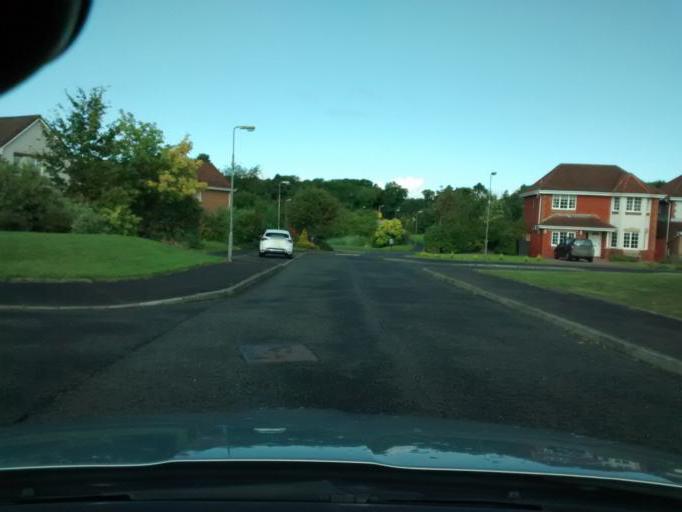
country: GB
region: Scotland
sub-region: West Lothian
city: Livingston
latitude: 55.8947
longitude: -3.5464
